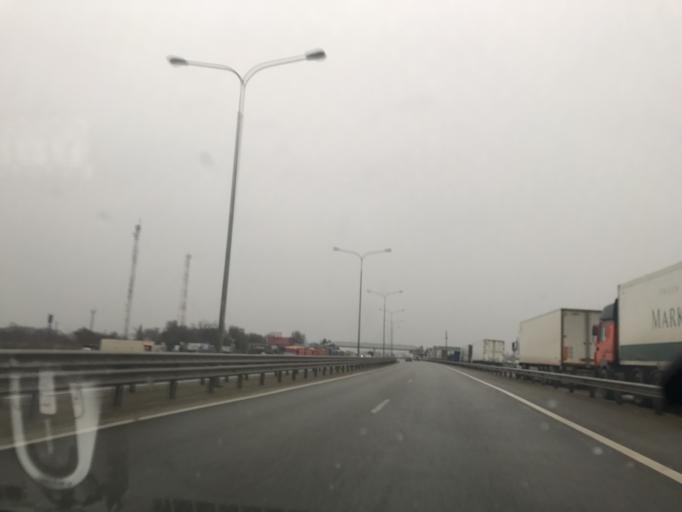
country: RU
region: Krasnodarskiy
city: Krylovskaya
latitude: 46.2825
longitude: 39.8304
